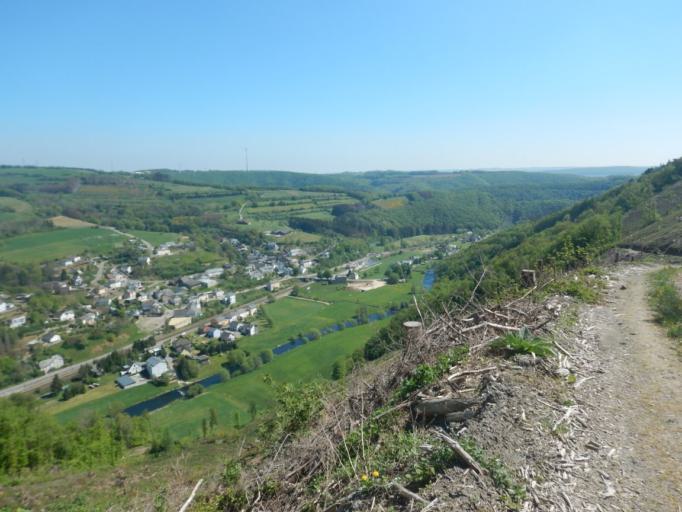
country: LU
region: Diekirch
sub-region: Canton de Diekirch
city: Bourscheid
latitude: 49.8989
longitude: 6.0806
